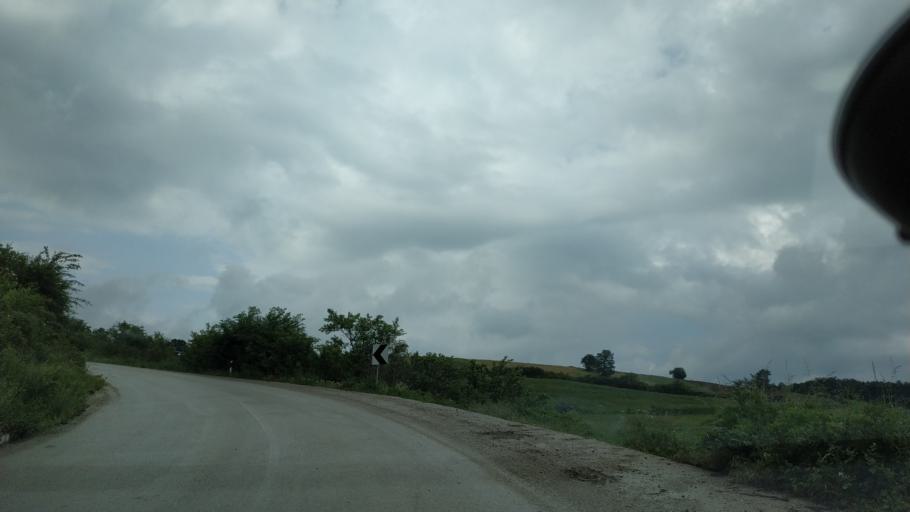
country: RS
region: Central Serbia
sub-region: Toplicki Okrug
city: Prokuplje
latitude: 43.4044
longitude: 21.5600
